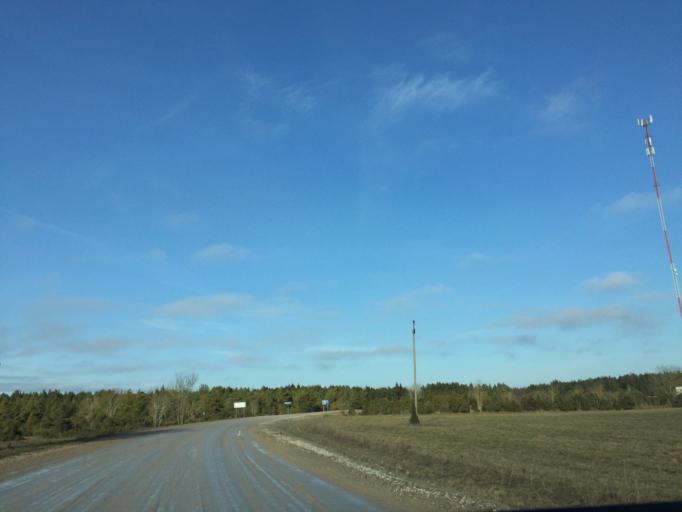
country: EE
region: Saare
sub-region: Kuressaare linn
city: Kuressaare
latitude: 58.4670
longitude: 22.0017
